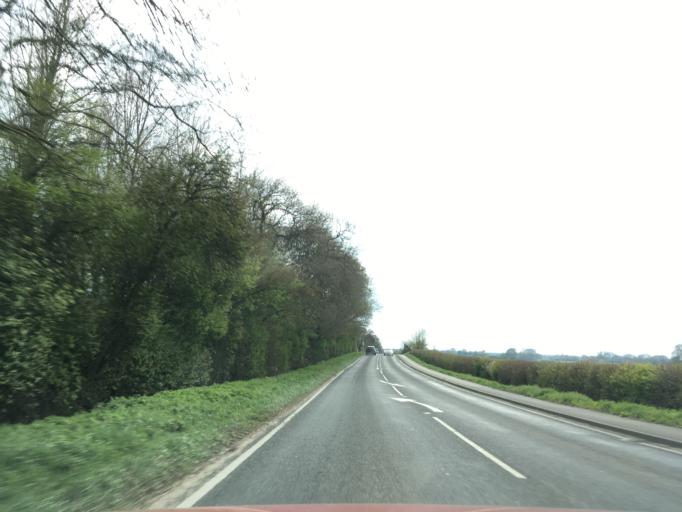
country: GB
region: England
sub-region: Oxfordshire
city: North Leigh
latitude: 51.8046
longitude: -1.4479
